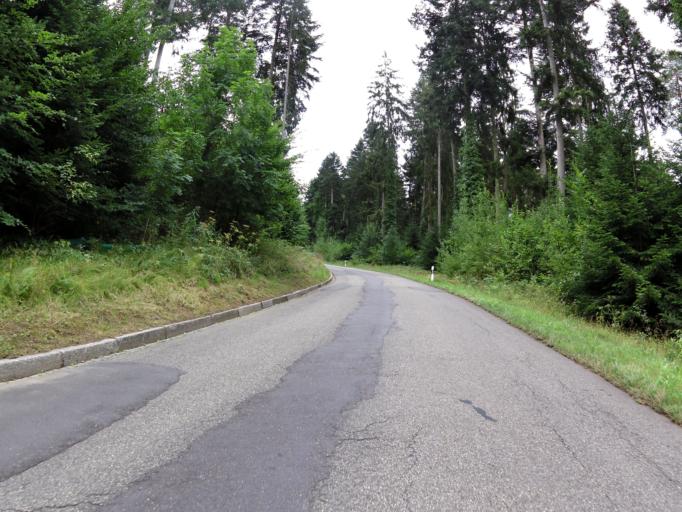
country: DE
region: Baden-Wuerttemberg
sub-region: Freiburg Region
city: Hohberg
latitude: 48.3356
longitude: 7.8941
